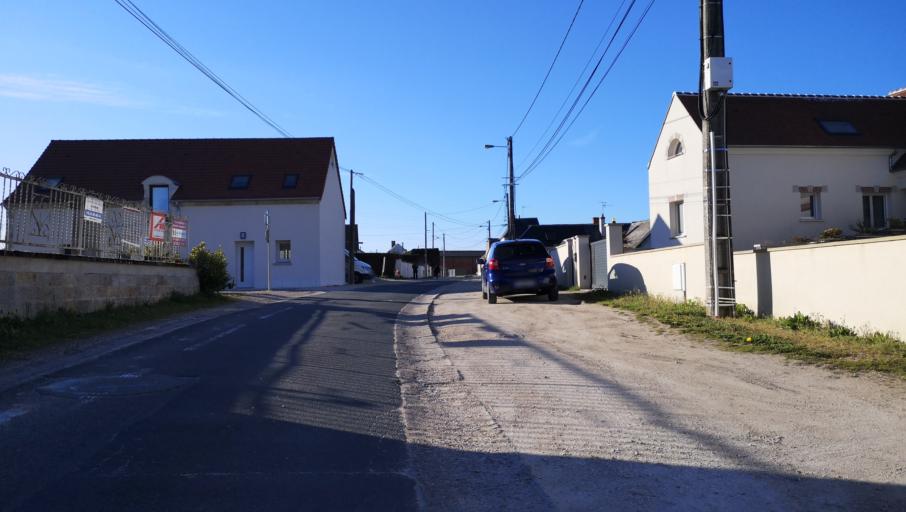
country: FR
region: Centre
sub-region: Departement du Loiret
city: Saint-Jean-de-Braye
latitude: 47.9206
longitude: 1.9757
